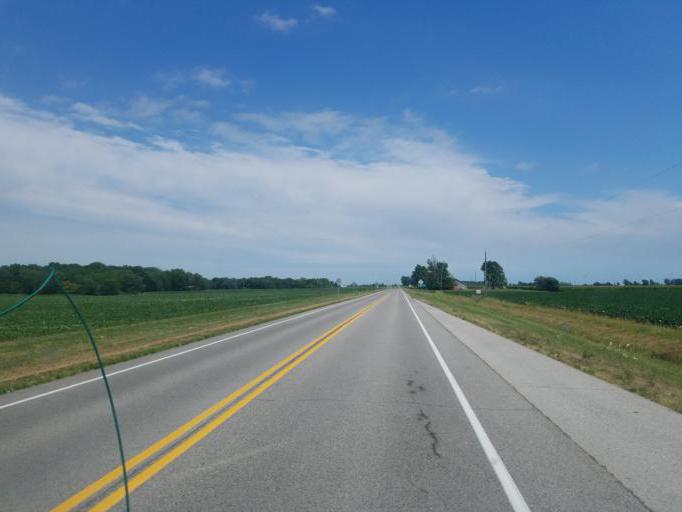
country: US
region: Indiana
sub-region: Allen County
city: Woodburn
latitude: 41.1542
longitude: -84.8469
